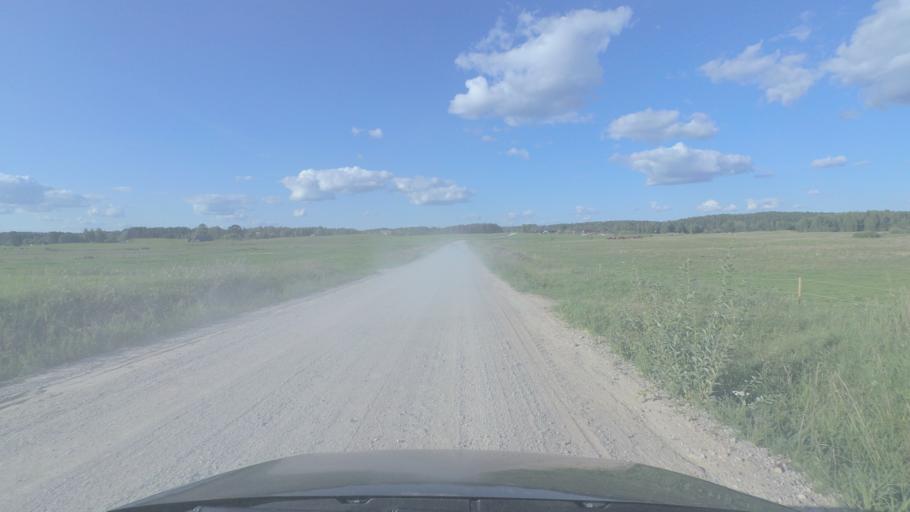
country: LT
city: Pabrade
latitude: 55.1328
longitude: 25.7069
